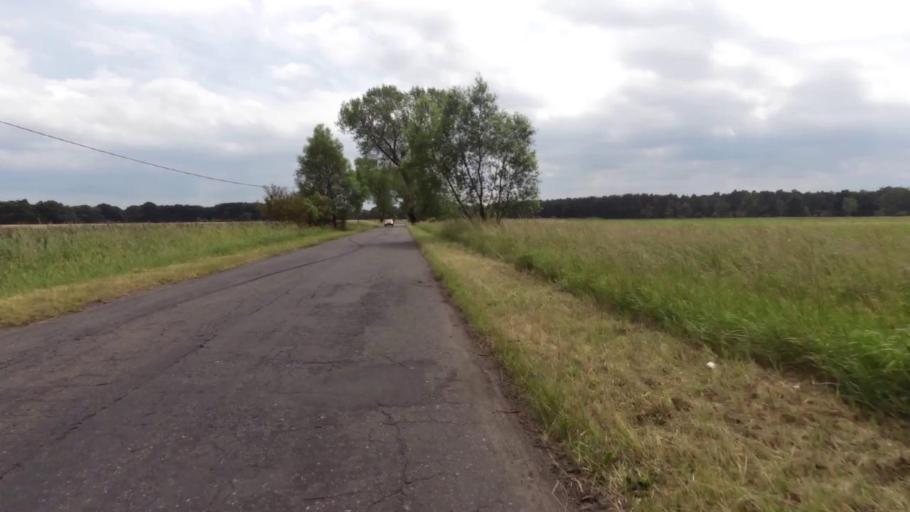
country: PL
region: West Pomeranian Voivodeship
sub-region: Powiat goleniowski
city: Stepnica
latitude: 53.7187
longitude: 14.5549
